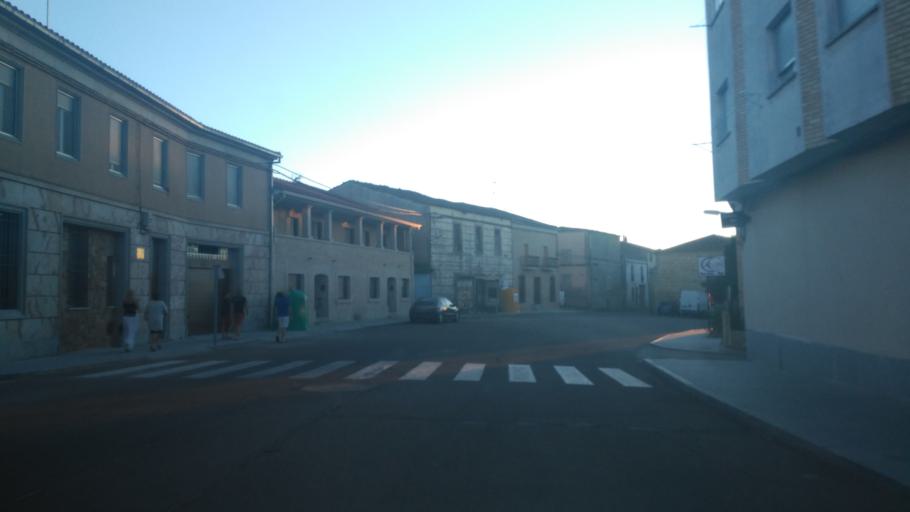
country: ES
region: Castille and Leon
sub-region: Provincia de Salamanca
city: Aldeadavila de la Ribera
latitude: 41.2176
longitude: -6.6153
